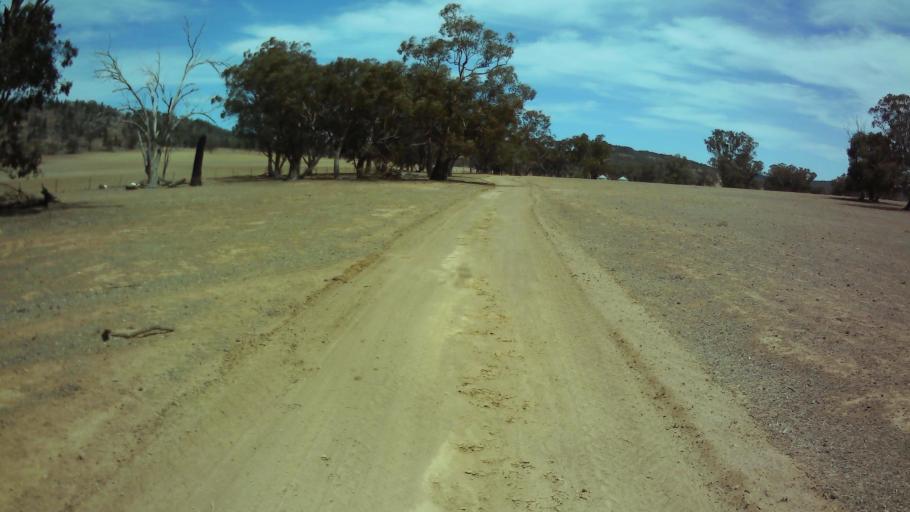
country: AU
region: New South Wales
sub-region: Weddin
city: Grenfell
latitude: -33.7736
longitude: 148.1519
